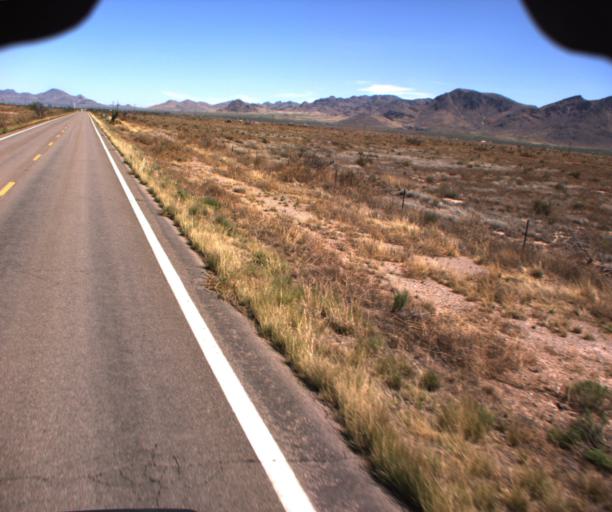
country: US
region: New Mexico
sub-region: Hidalgo County
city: Lordsburg
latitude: 31.8050
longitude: -109.0532
